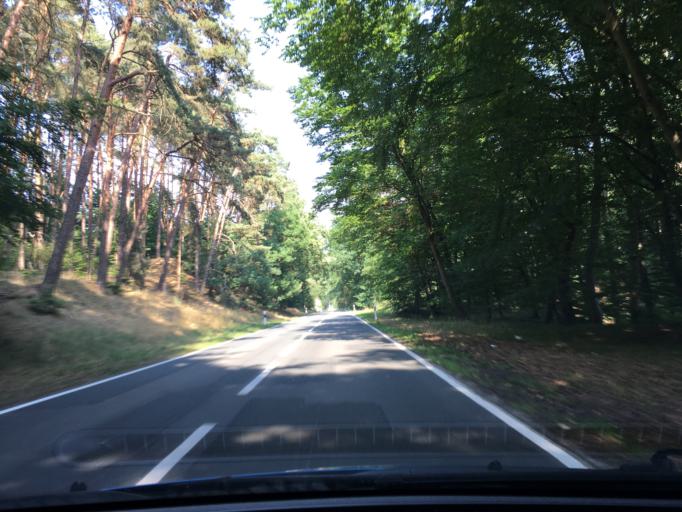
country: DE
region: Lower Saxony
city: Tosterglope
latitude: 53.2367
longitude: 10.8383
